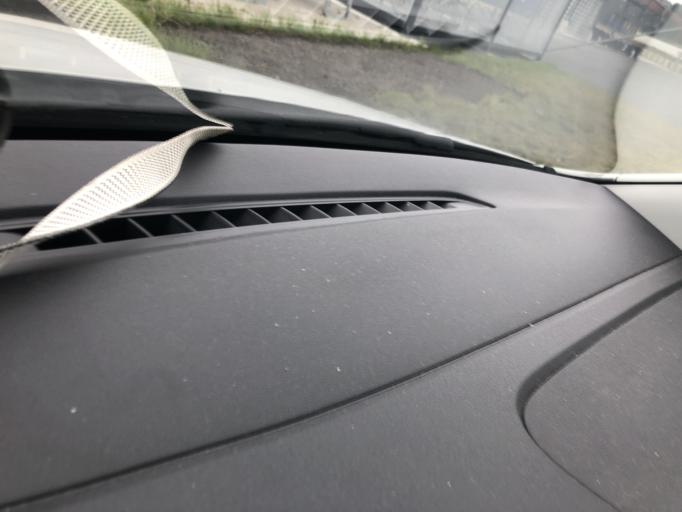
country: SE
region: Vaestra Goetaland
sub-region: Goteborg
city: Majorna
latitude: 57.7364
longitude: 11.8689
